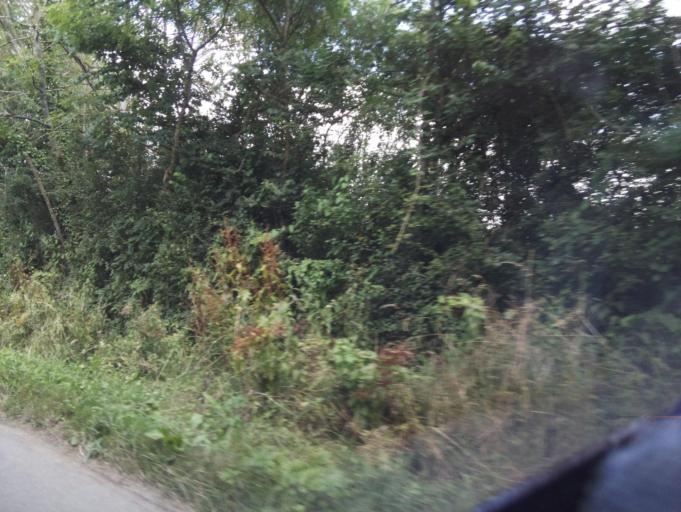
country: GB
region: England
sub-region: Wiltshire
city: Minety
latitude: 51.6148
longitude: -1.9868
